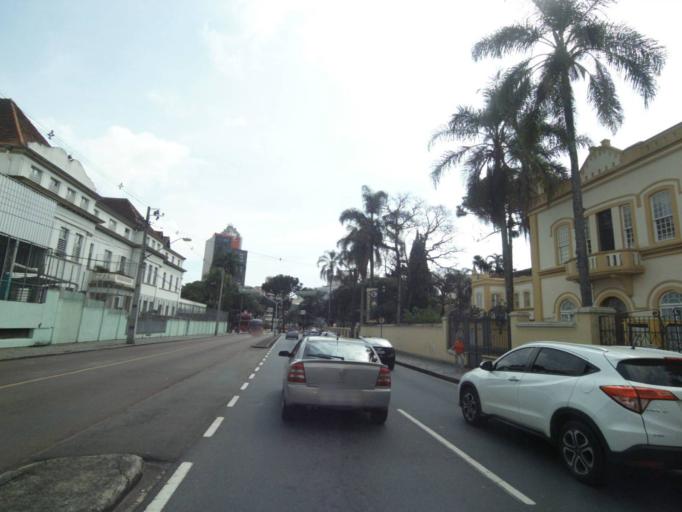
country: BR
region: Parana
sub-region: Curitiba
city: Curitiba
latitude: -25.4375
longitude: -49.2730
